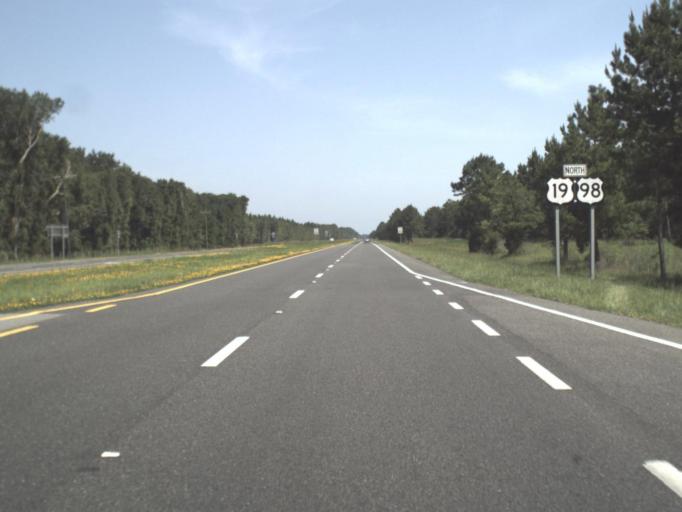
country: US
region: Florida
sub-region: Levy County
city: Chiefland
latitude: 29.4172
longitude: -82.8234
